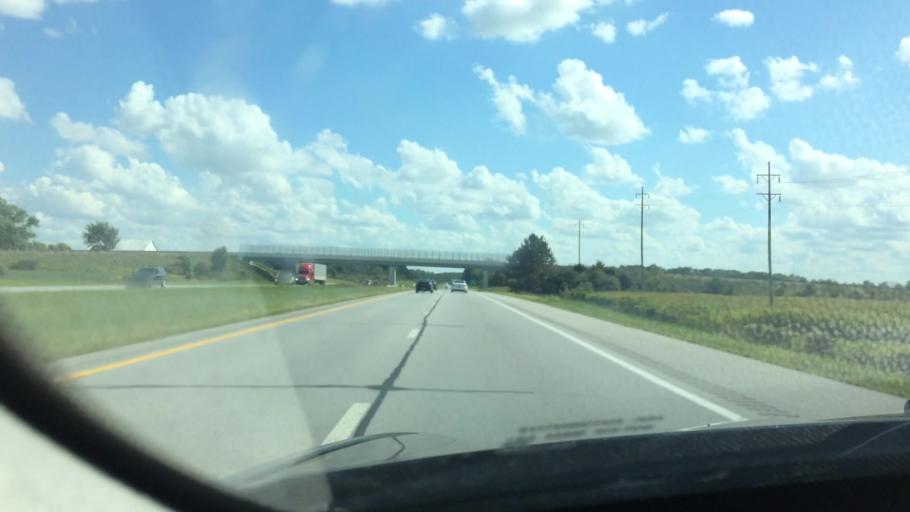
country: US
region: Ohio
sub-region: Shelby County
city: Anna
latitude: 40.3479
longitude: -84.1600
